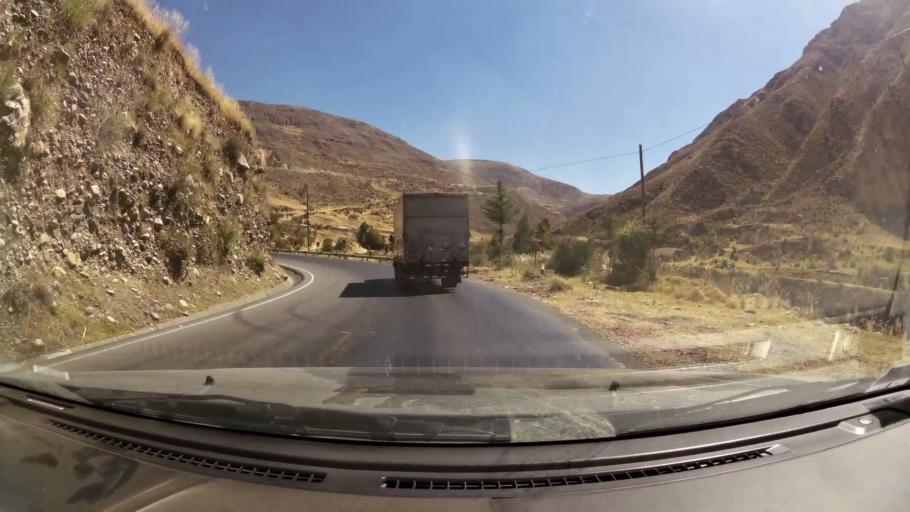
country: PE
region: Junin
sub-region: Provincia de Jauja
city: Parco
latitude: -11.7833
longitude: -75.5755
